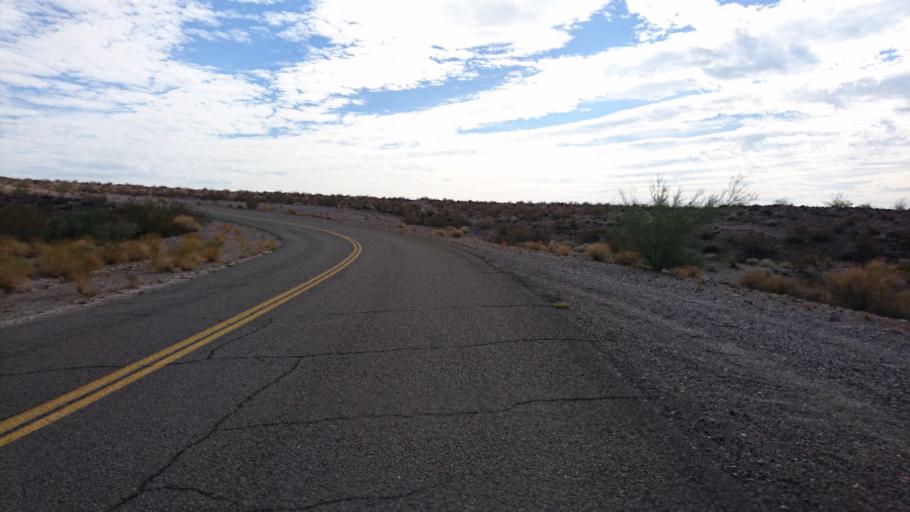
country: US
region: Arizona
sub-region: Mohave County
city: Mohave Valley
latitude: 34.9055
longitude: -114.4299
